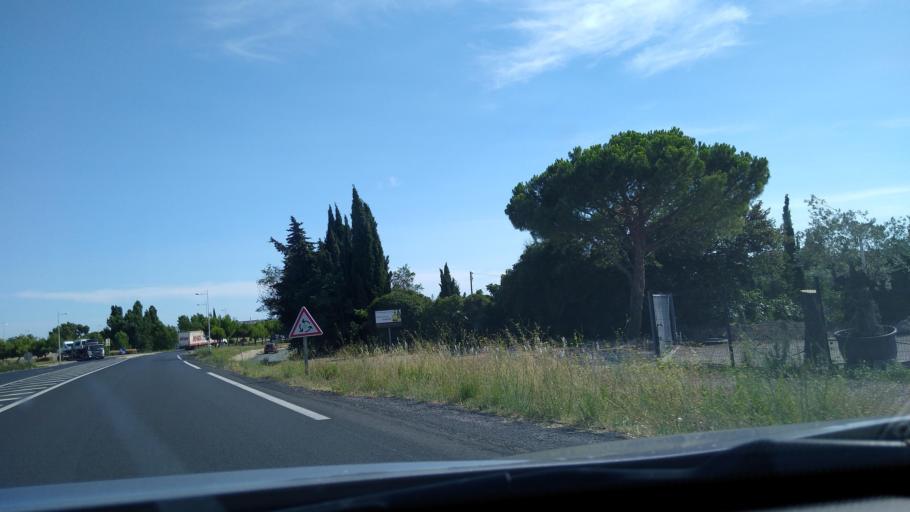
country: FR
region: Languedoc-Roussillon
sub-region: Departement de l'Herault
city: Sete
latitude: 43.4259
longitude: 3.7225
